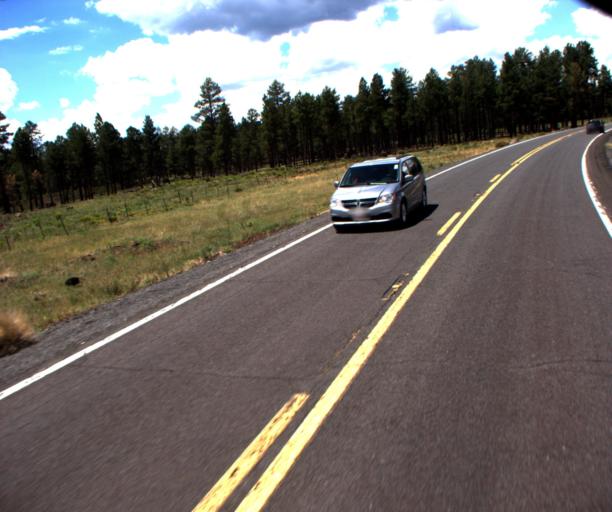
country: US
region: Arizona
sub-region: Coconino County
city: Parks
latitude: 35.4507
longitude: -111.7725
